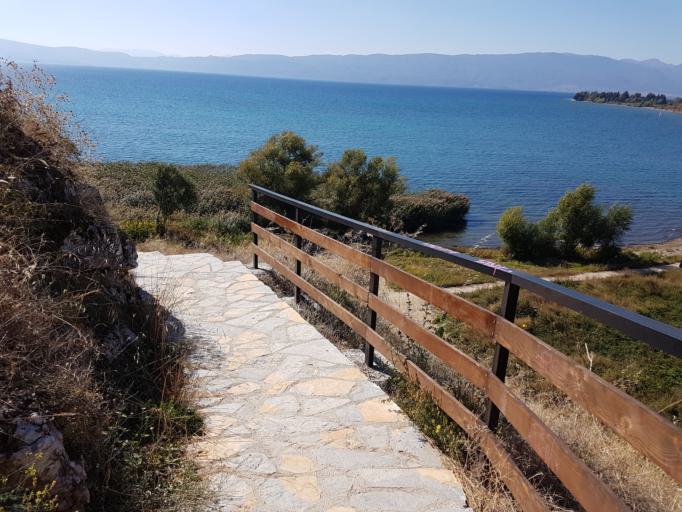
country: MK
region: Ohrid
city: Ohrid
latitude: 41.1161
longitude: 20.7891
